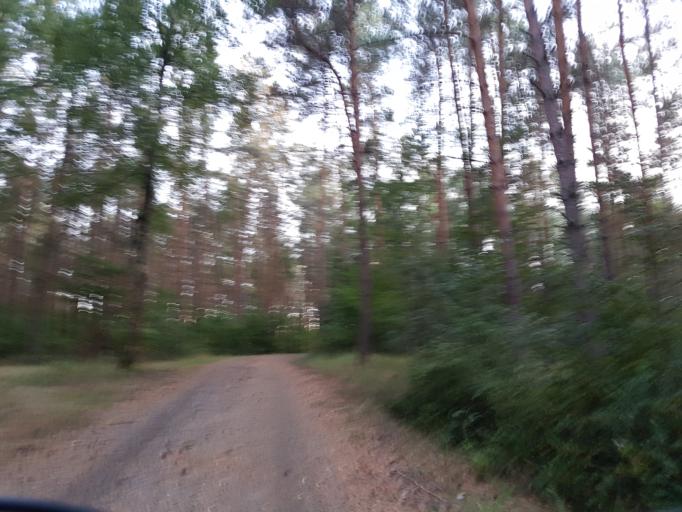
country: DE
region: Brandenburg
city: Trobitz
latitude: 51.5786
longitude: 13.4530
